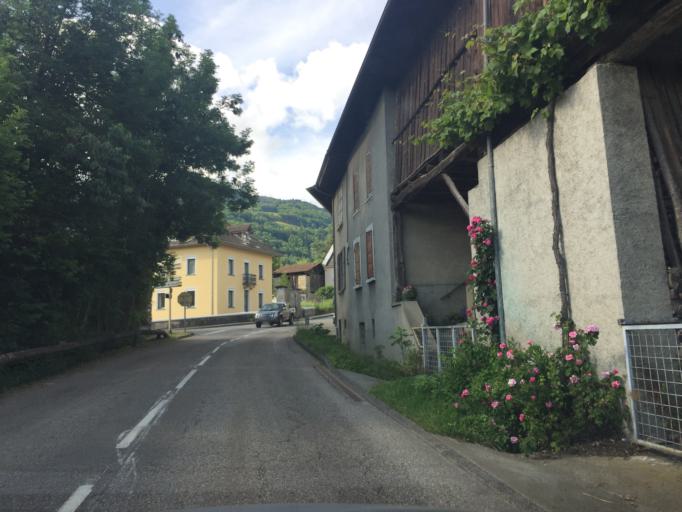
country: FR
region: Rhone-Alpes
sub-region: Departement de la Savoie
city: La Rochette
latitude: 45.4442
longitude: 6.1218
